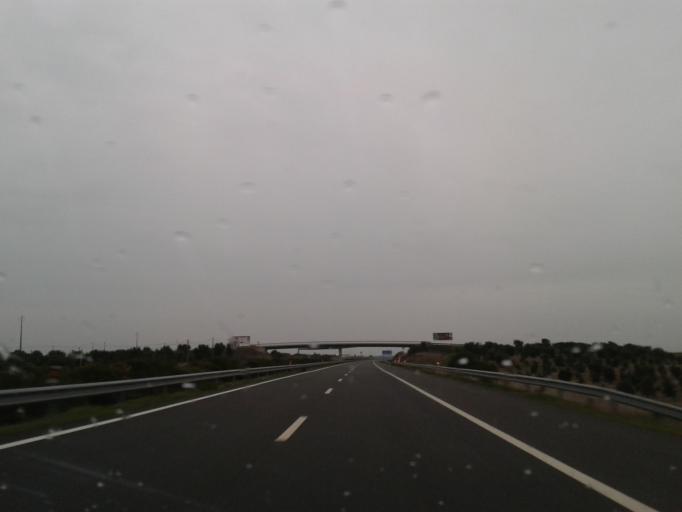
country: PT
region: Beja
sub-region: Aljustrel
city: Aljustrel
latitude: 37.9146
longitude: -8.2422
